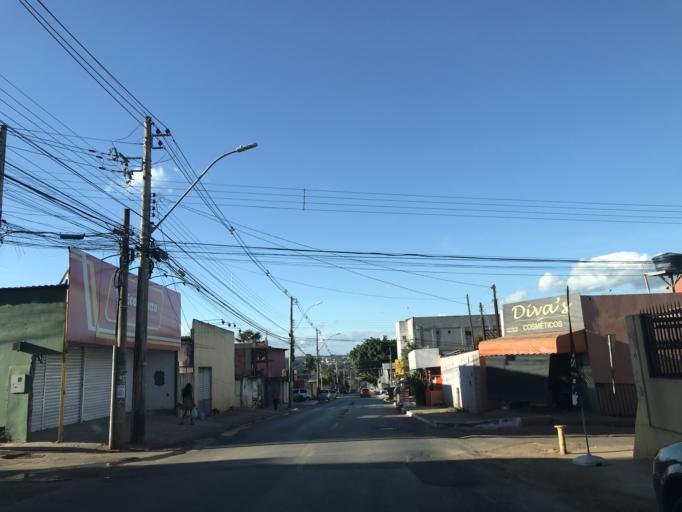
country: BR
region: Federal District
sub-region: Brasilia
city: Brasilia
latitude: -15.8958
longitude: -47.7860
